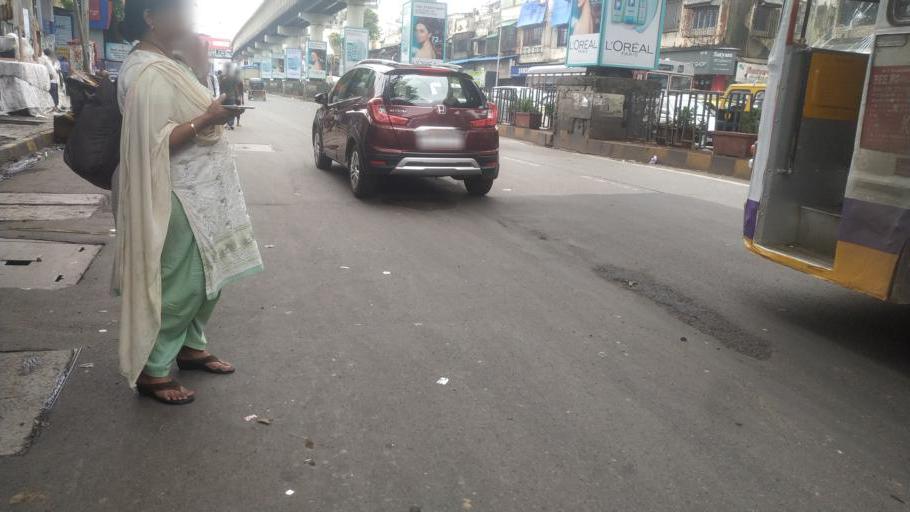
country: IN
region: Maharashtra
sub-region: Mumbai Suburban
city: Mumbai
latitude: 19.0539
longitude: 72.8380
